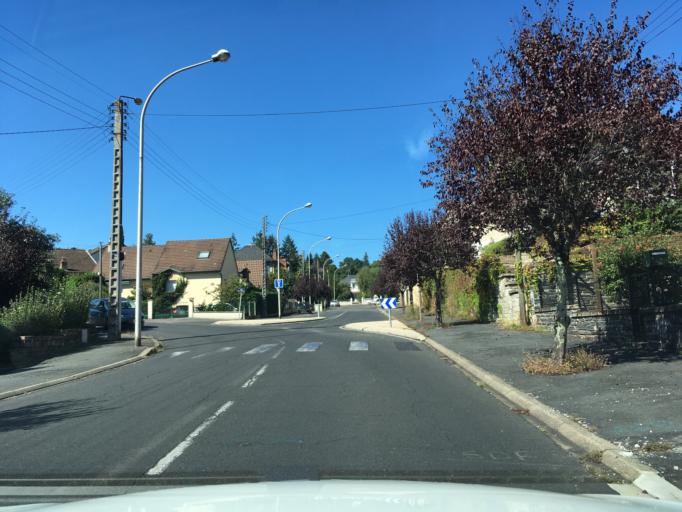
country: FR
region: Limousin
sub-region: Departement de la Correze
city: Brive-la-Gaillarde
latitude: 45.1668
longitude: 1.5194
